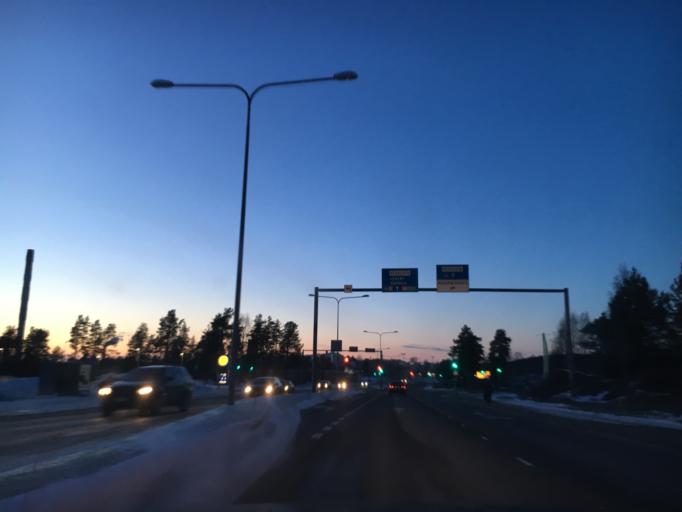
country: FI
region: Kainuu
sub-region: Kajaani
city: Kajaani
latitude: 64.2168
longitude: 27.7311
